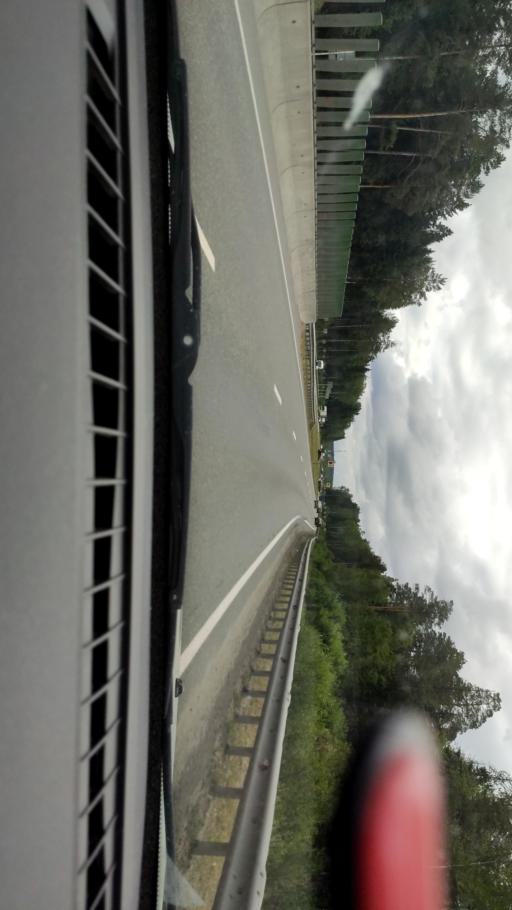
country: RU
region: Perm
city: Kondratovo
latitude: 58.0426
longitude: 55.9999
